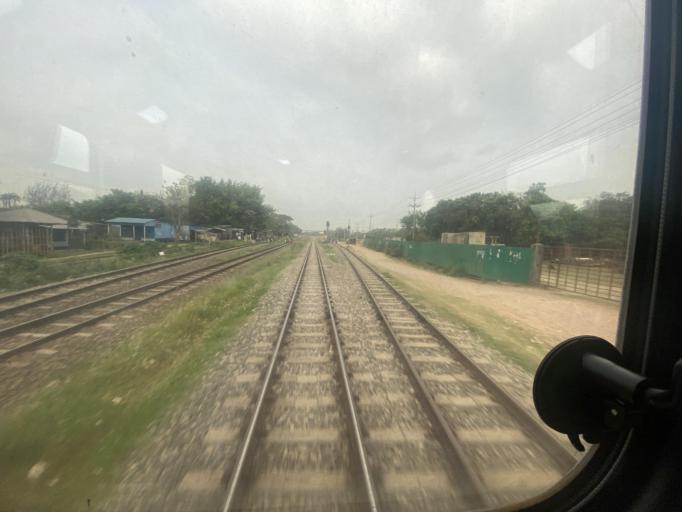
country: BD
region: Dhaka
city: Tungi
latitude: 23.9365
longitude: 90.4800
